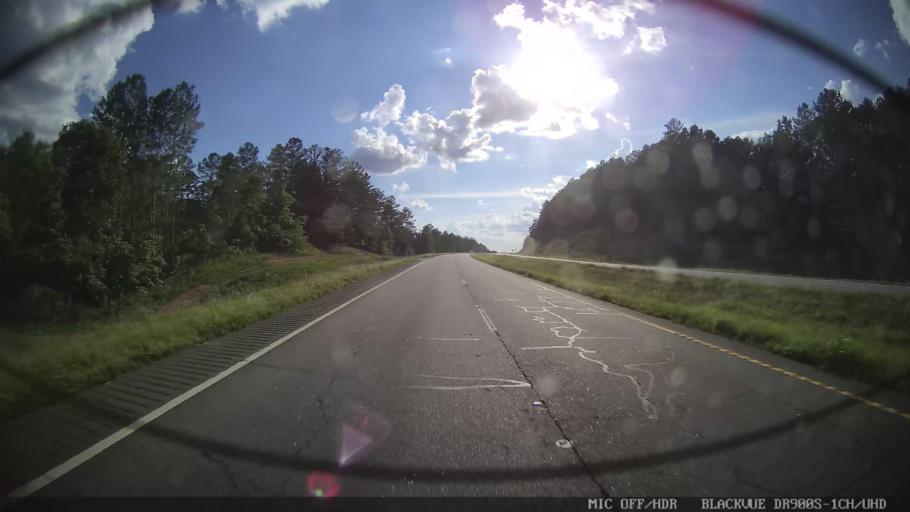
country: US
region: Georgia
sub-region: Bartow County
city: Euharlee
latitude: 34.2035
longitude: -85.0184
